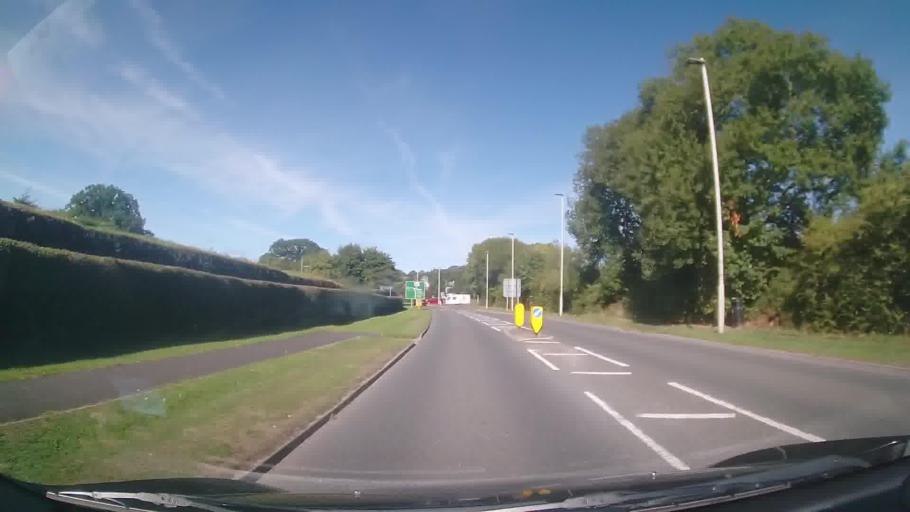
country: GB
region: Wales
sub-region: Sir Powys
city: Hay
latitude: 52.0040
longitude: -3.2426
